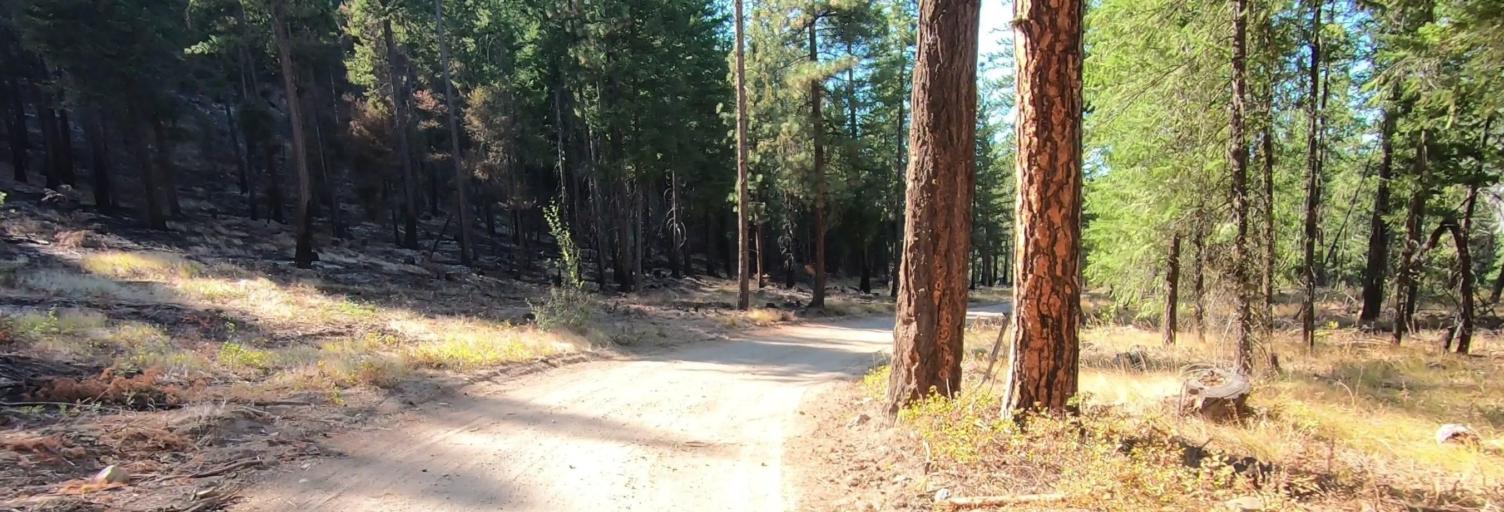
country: US
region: Washington
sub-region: Chelan County
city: Granite Falls
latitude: 48.5162
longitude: -120.2987
